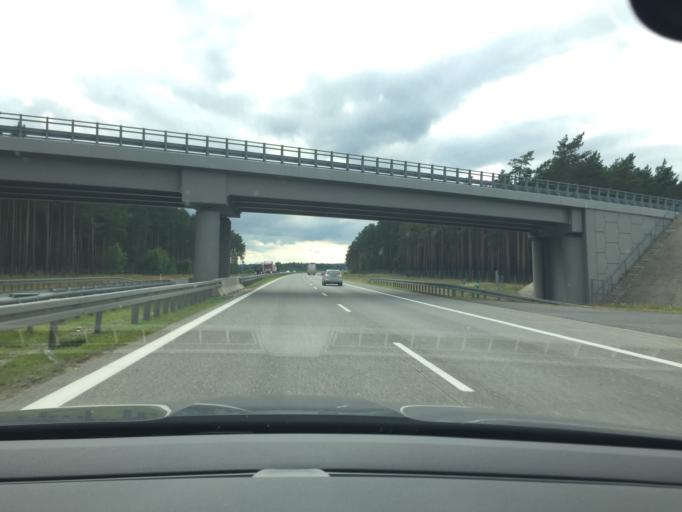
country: PL
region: Lubusz
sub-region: Powiat swiebodzinski
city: Szczaniec
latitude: 52.2968
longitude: 15.7147
